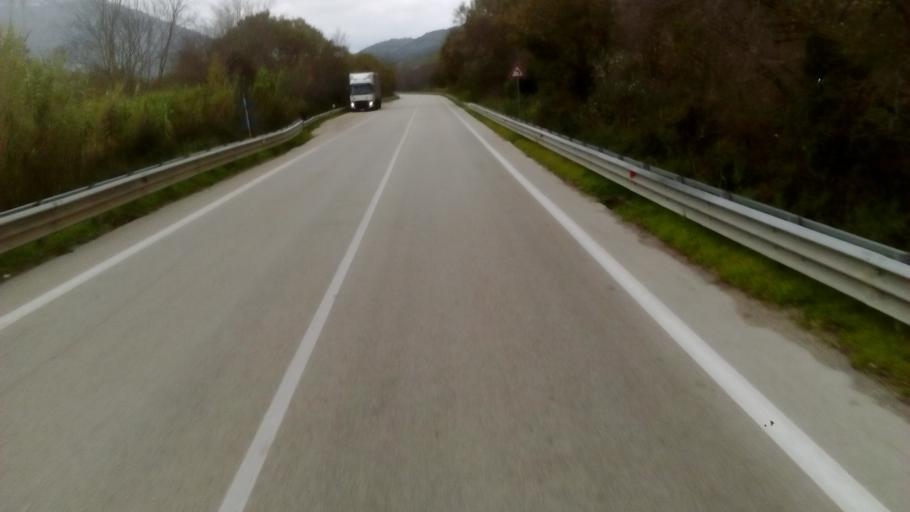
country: IT
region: Abruzzo
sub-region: Provincia di Chieti
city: Celenza sul Trigno
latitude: 41.8784
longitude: 14.6055
